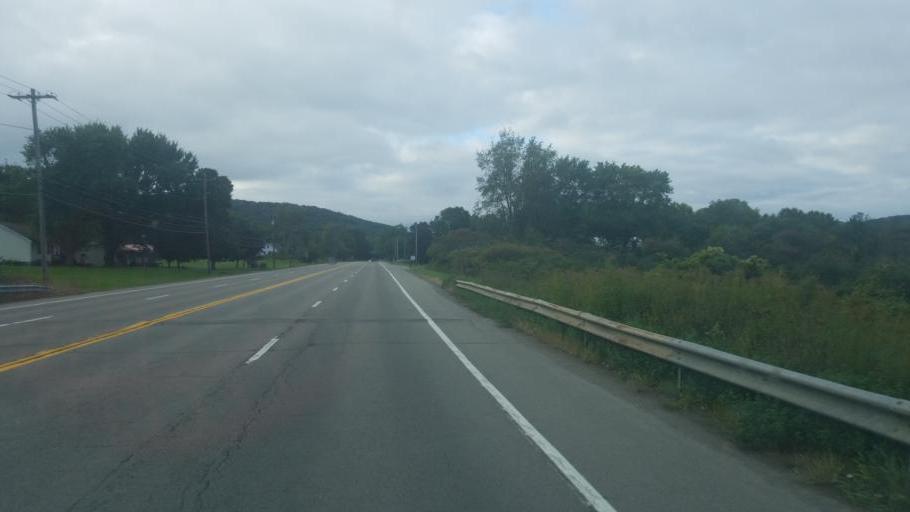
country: US
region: New York
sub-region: Cattaraugus County
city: Olean
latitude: 42.1425
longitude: -78.4005
